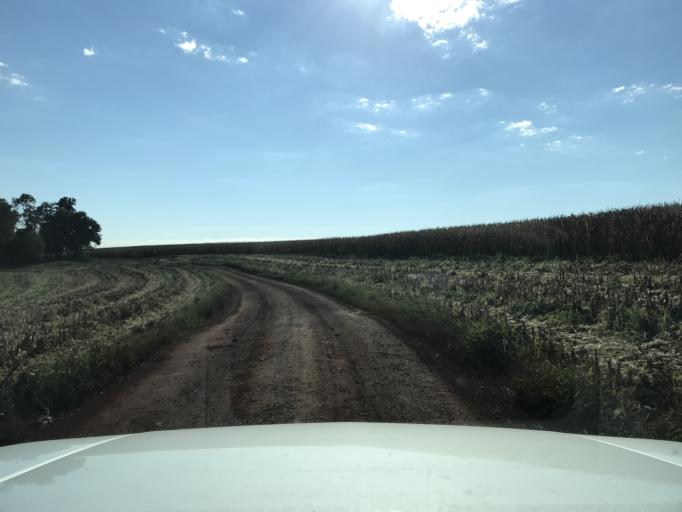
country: BR
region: Parana
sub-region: Palotina
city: Palotina
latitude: -24.2703
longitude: -53.8153
